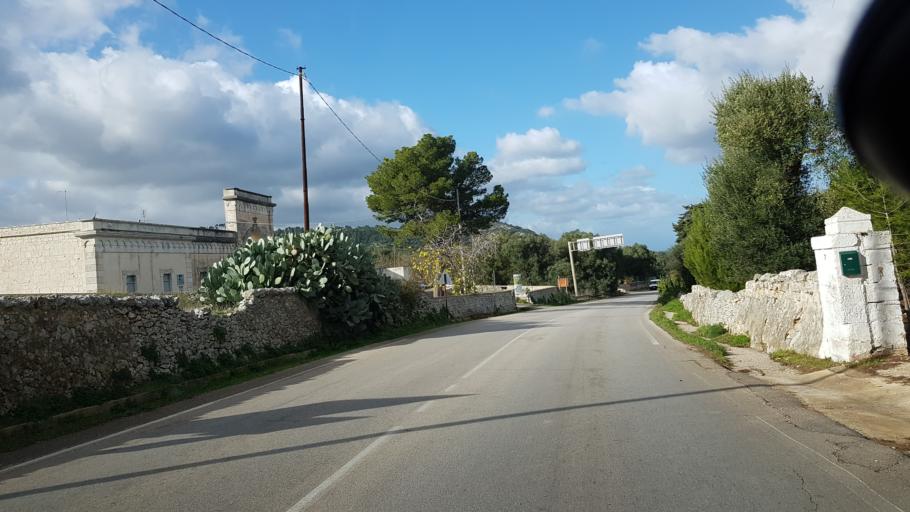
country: IT
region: Apulia
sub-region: Provincia di Brindisi
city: Ostuni
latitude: 40.7333
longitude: 17.5679
